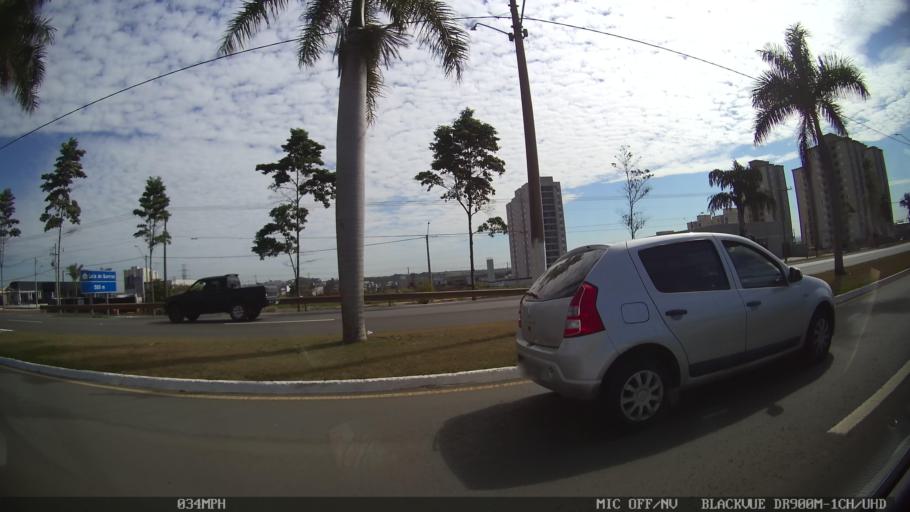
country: BR
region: Sao Paulo
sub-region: Santa Barbara D'Oeste
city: Santa Barbara d'Oeste
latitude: -22.7613
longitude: -47.4329
